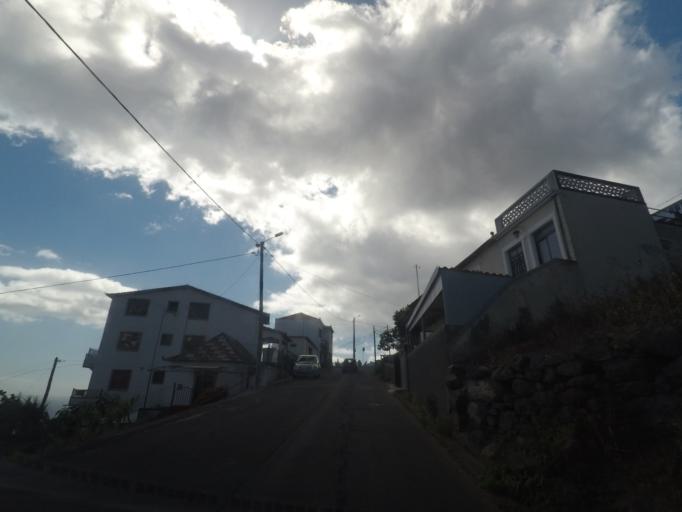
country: PT
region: Madeira
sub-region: Ribeira Brava
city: Campanario
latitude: 32.6730
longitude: -17.0491
